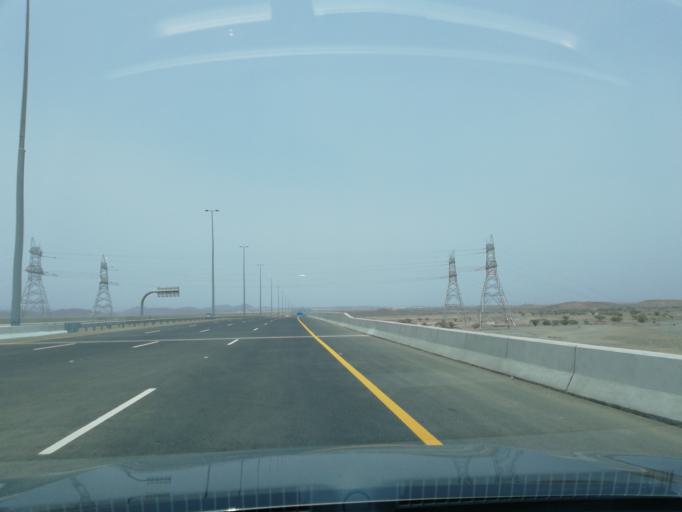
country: OM
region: Al Batinah
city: Al Liwa'
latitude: 24.4272
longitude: 56.5285
